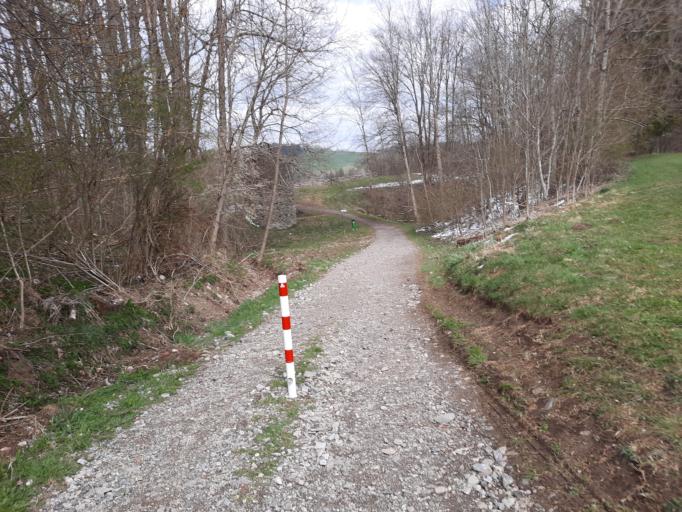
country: DE
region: Bavaria
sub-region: Swabia
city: Altusried
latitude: 47.8233
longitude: 10.1998
